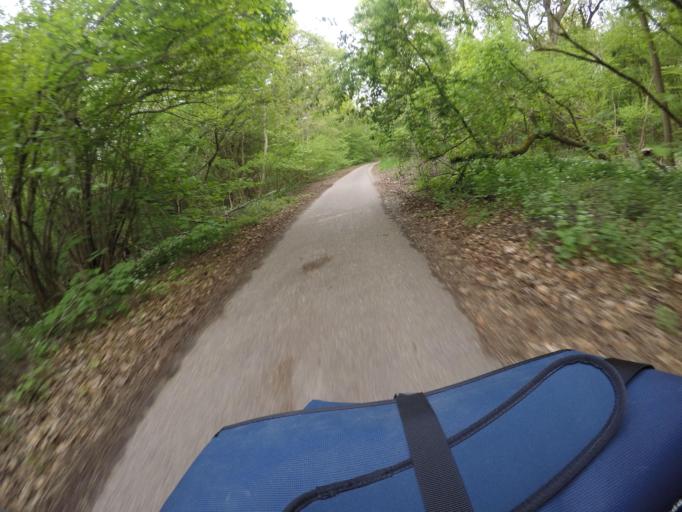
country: FR
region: Alsace
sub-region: Departement du Bas-Rhin
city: Eschau
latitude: 48.5051
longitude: 7.7470
